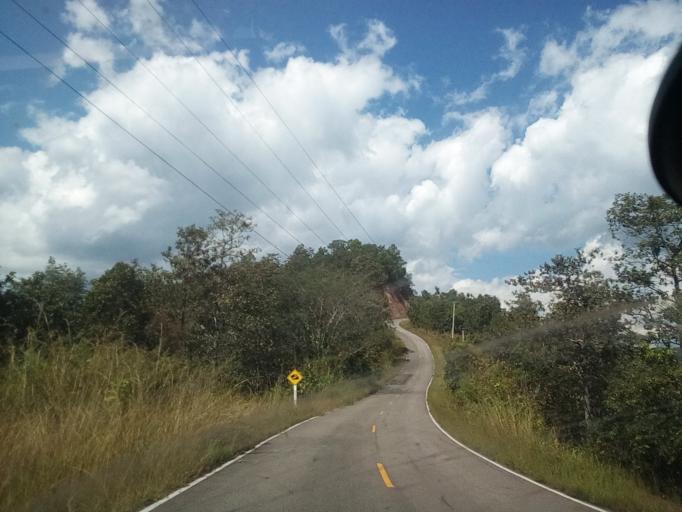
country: TH
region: Chiang Mai
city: Samoeng
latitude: 18.8655
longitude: 98.6939
